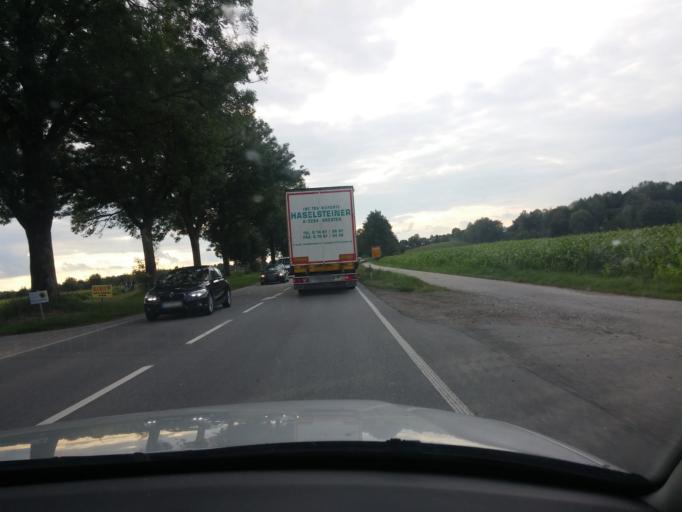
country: DE
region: Bavaria
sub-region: Upper Bavaria
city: Zorneding
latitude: 48.0828
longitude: 11.8492
